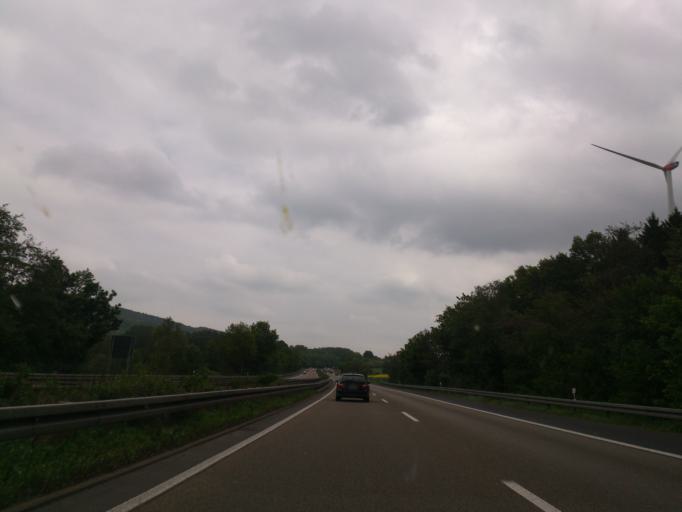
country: DE
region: Hesse
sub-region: Regierungsbezirk Kassel
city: Martinhagen
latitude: 51.3060
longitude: 9.3078
